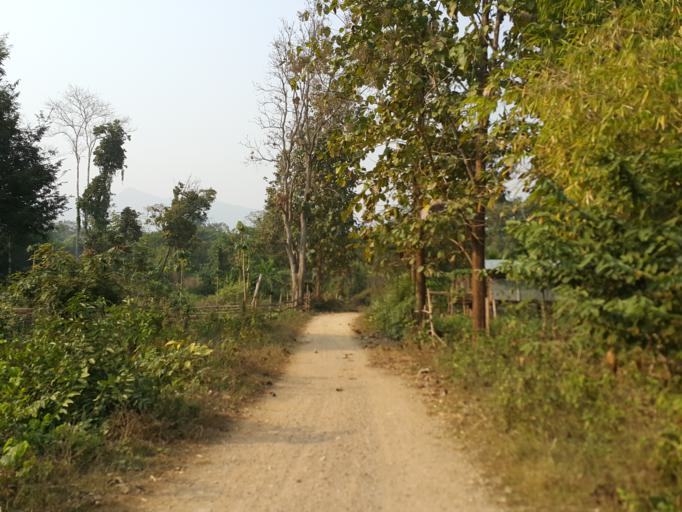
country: TH
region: Lamphun
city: Li
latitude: 17.6048
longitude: 98.9637
